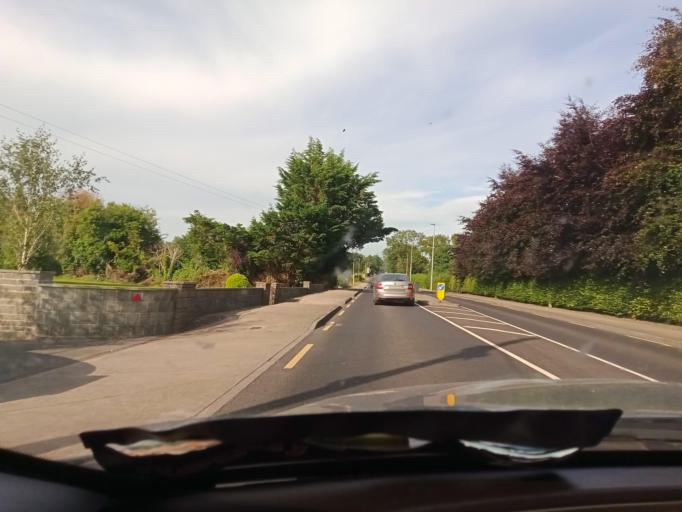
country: IE
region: Ulster
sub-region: An Cabhan
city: Cavan
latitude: 53.9365
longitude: -7.4017
